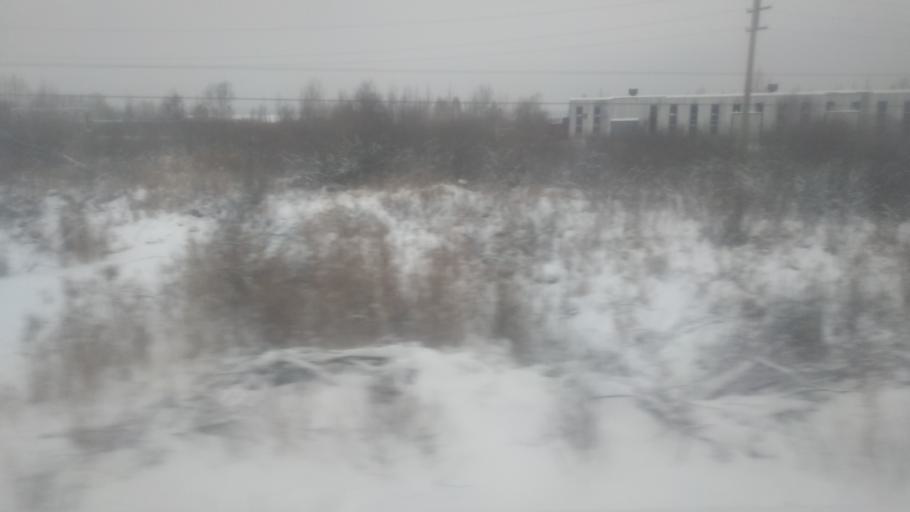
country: RU
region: Bashkortostan
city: Amzya
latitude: 56.2455
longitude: 54.6148
